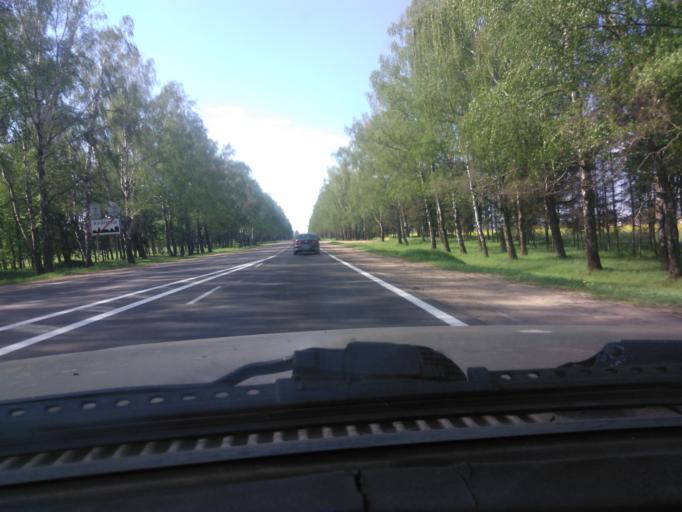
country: BY
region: Mogilev
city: Buynichy
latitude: 53.8476
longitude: 30.2516
